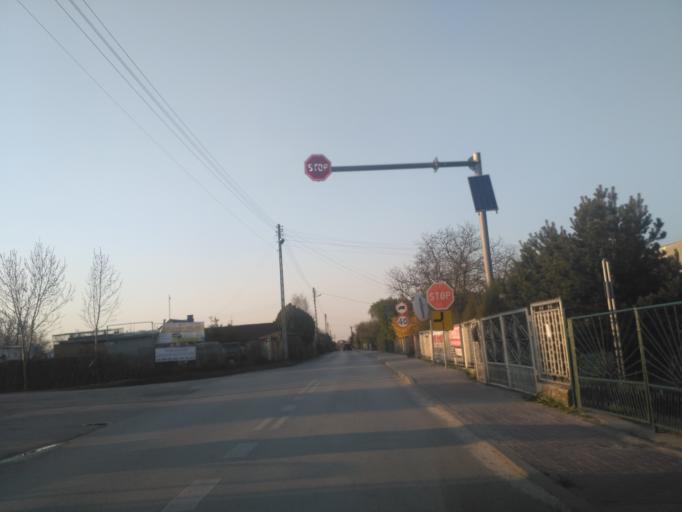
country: PL
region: Lublin Voivodeship
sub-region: Powiat chelmski
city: Pokrowka
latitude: 51.1131
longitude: 23.4835
